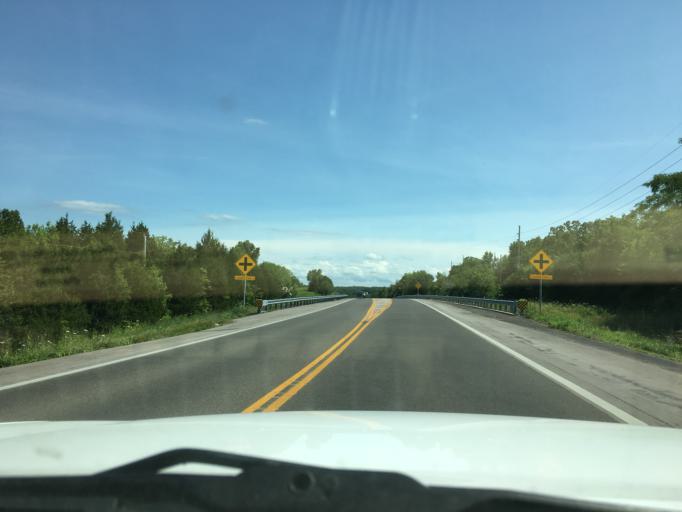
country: US
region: Missouri
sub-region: Franklin County
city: Washington
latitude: 38.5077
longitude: -91.0059
